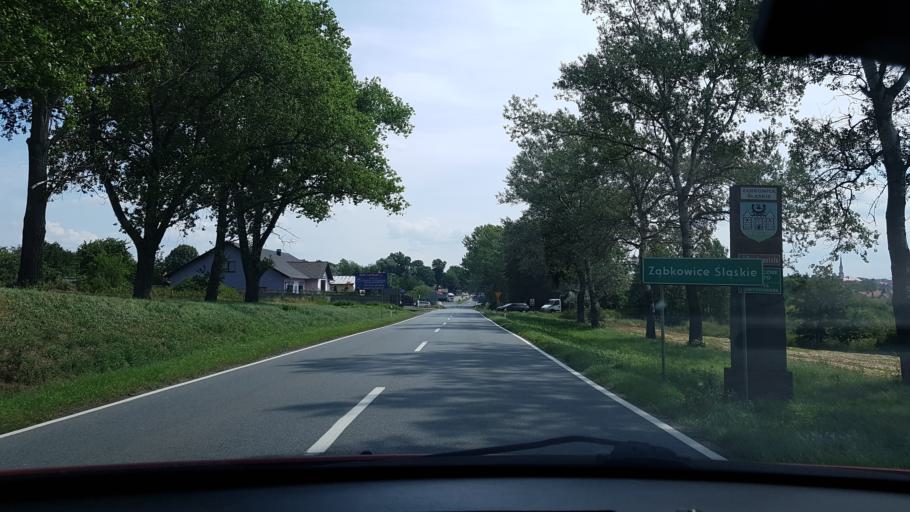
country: PL
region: Lower Silesian Voivodeship
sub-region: Powiat zabkowicki
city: Zabkowice Slaskie
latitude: 50.6012
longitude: 16.8012
